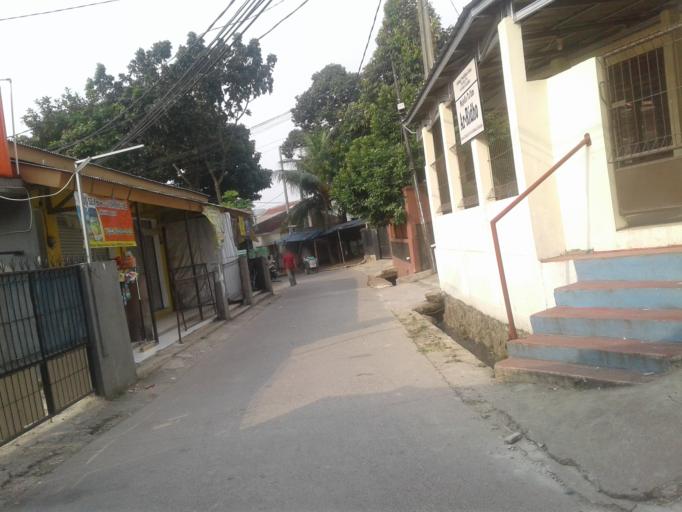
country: ID
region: West Java
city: Depok
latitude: -6.3761
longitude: 106.8366
